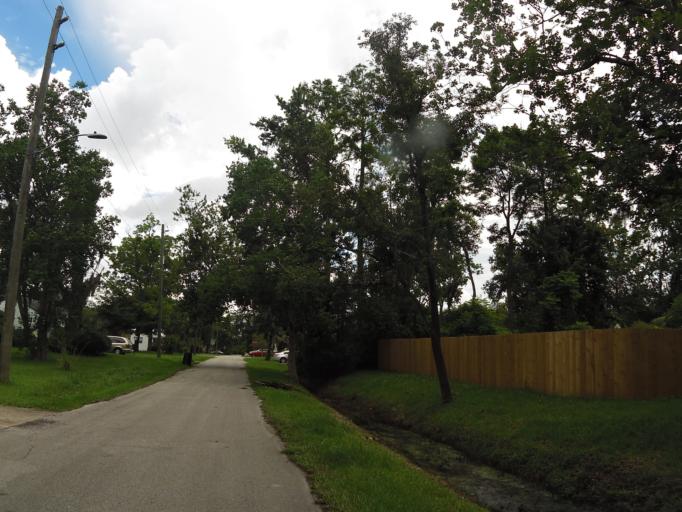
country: US
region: Florida
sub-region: Duval County
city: Jacksonville
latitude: 30.2875
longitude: -81.6458
